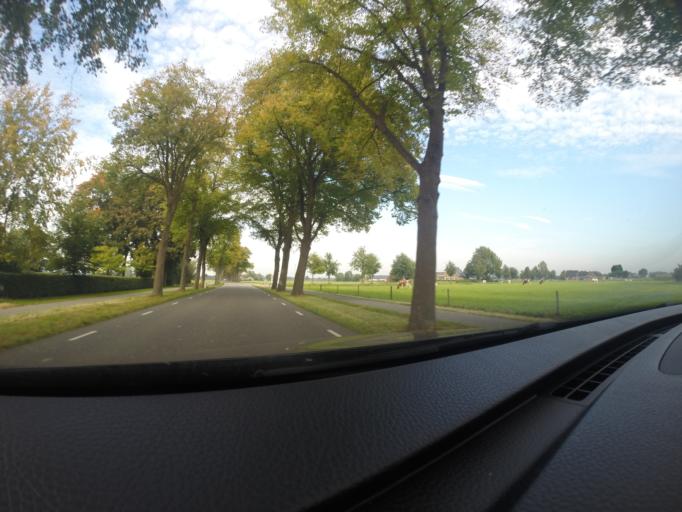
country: NL
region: Gelderland
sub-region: Gemeente Doetinchem
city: Doetinchem
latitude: 51.9699
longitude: 6.2133
